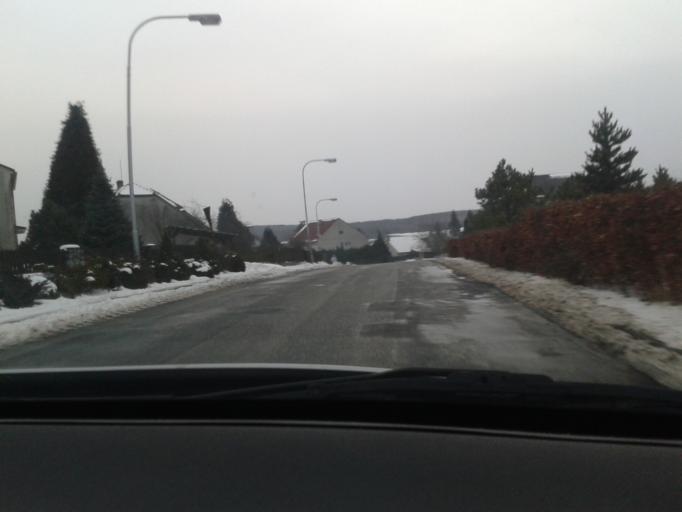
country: CZ
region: Olomoucky
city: Protivanov
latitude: 49.5310
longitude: 16.8623
